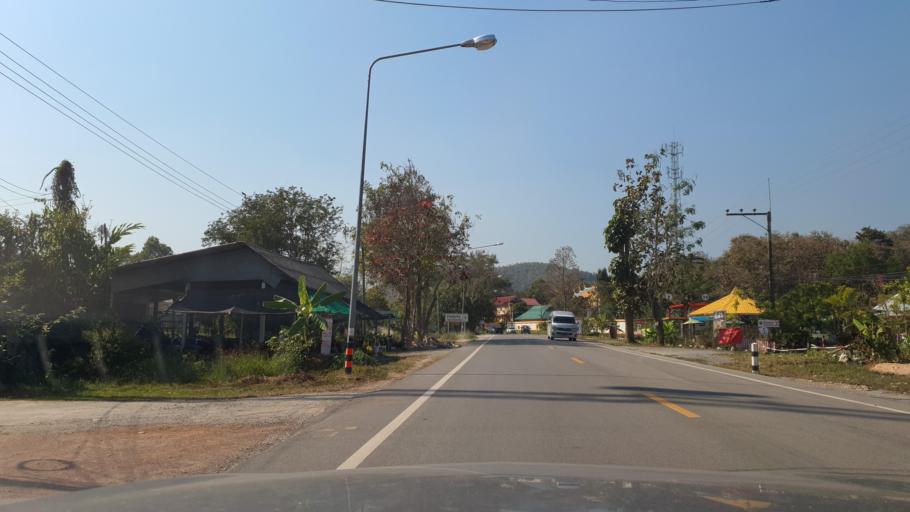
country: TH
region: Chiang Rai
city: Mae Lao
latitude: 19.8332
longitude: 99.7017
